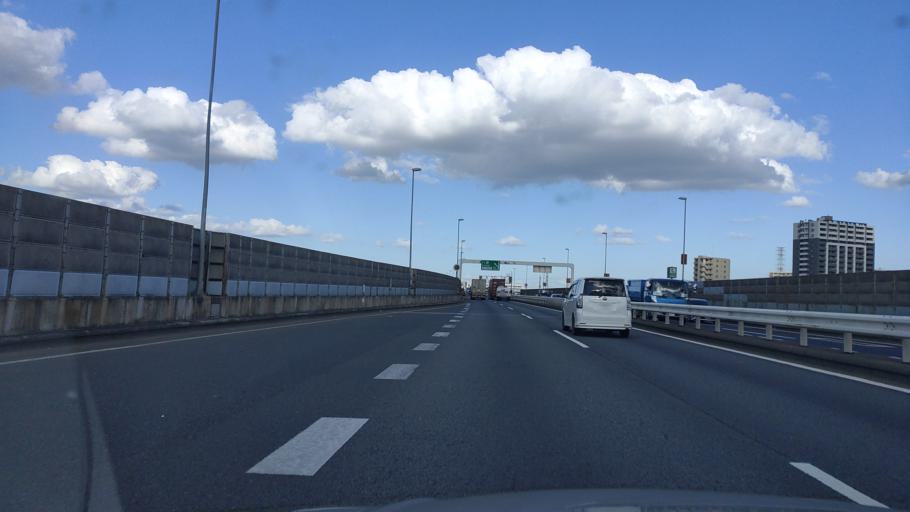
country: JP
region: Saitama
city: Yashio-shi
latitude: 35.8073
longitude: 139.8373
